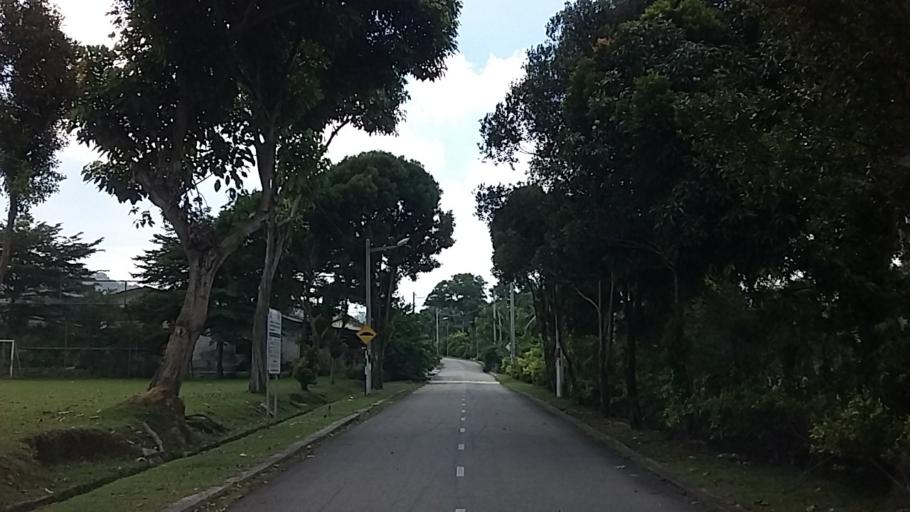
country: MY
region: Johor
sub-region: Daerah Batu Pahat
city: Batu Pahat
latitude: 1.8422
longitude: 102.9446
